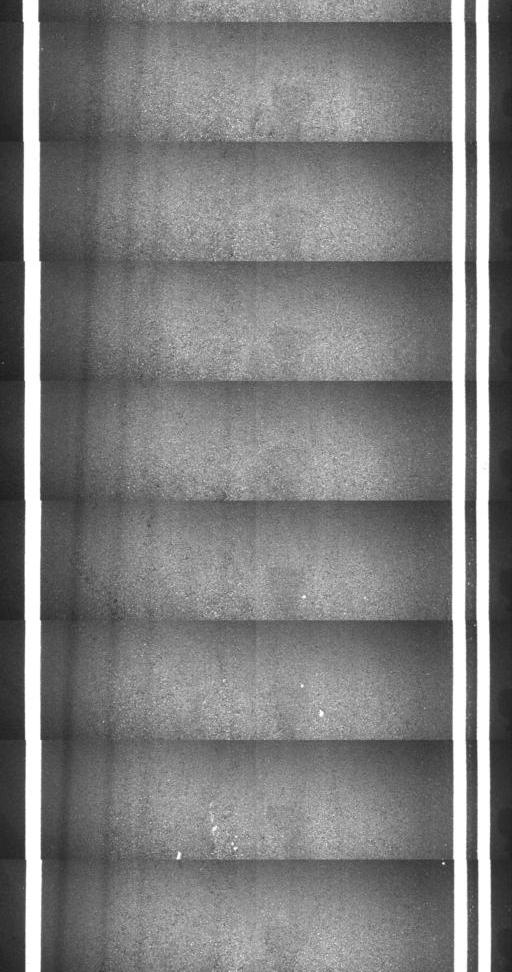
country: US
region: Vermont
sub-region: Chittenden County
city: Colchester
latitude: 44.5302
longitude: -73.1316
